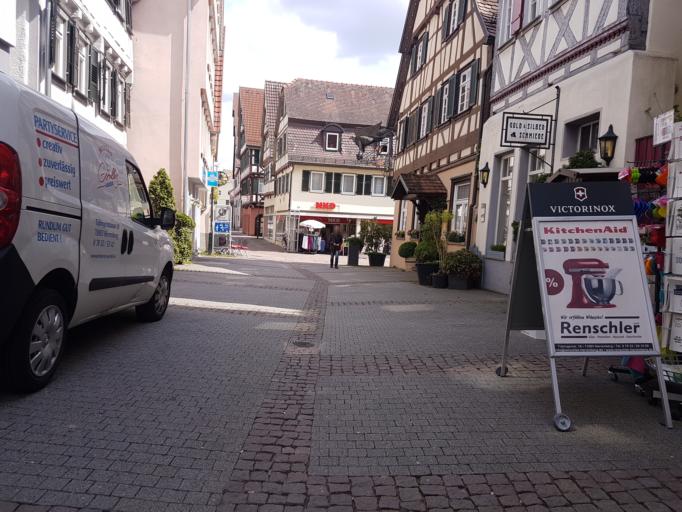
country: DE
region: Baden-Wuerttemberg
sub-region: Regierungsbezirk Stuttgart
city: Herrenberg
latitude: 48.5957
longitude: 8.8712
